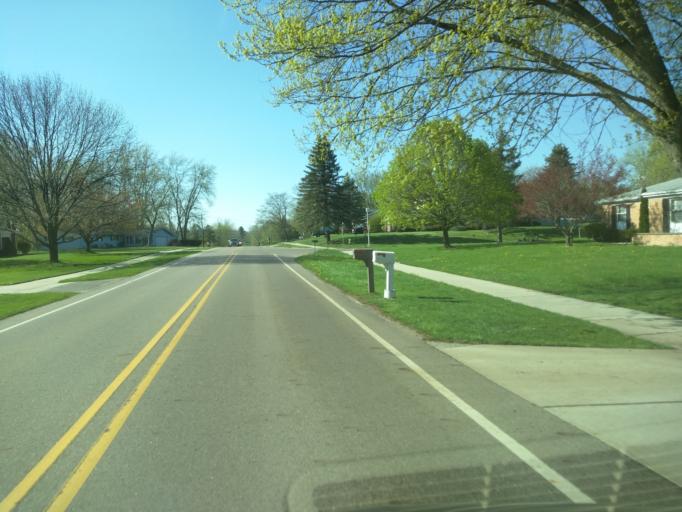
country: US
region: Michigan
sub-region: Eaton County
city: Waverly
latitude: 42.7573
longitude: -84.6462
